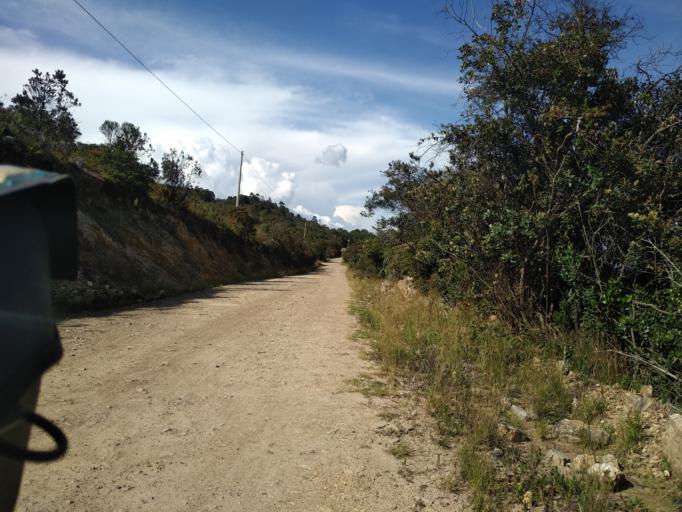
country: CO
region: Cundinamarca
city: Guacheta
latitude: 5.4545
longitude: -73.6479
